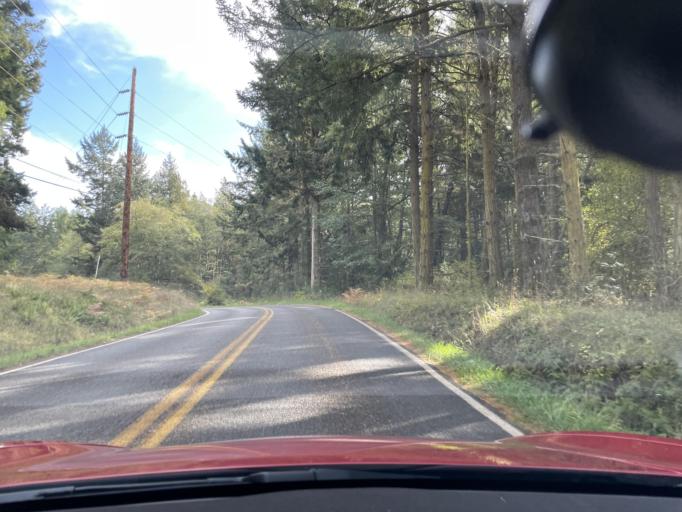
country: US
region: Washington
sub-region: San Juan County
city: Friday Harbor
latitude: 48.5188
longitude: -122.9953
